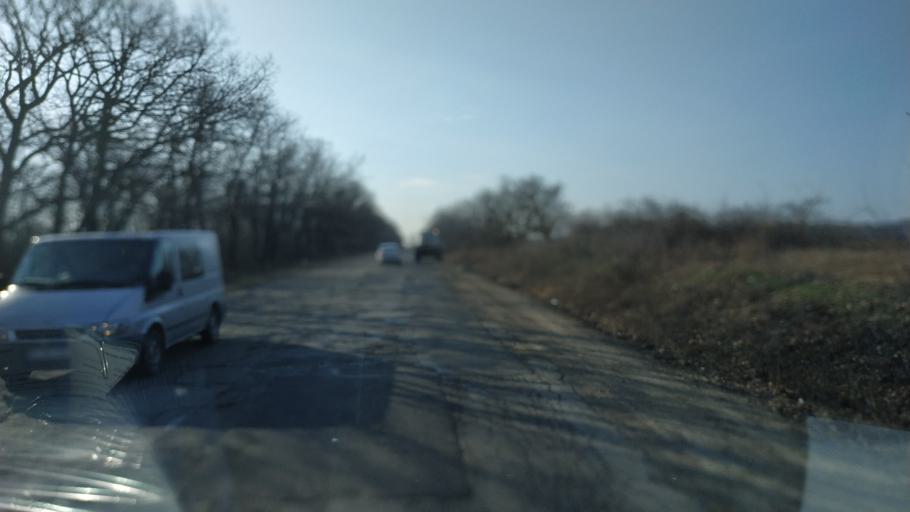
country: MD
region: Chisinau
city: Singera
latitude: 46.8712
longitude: 29.0398
